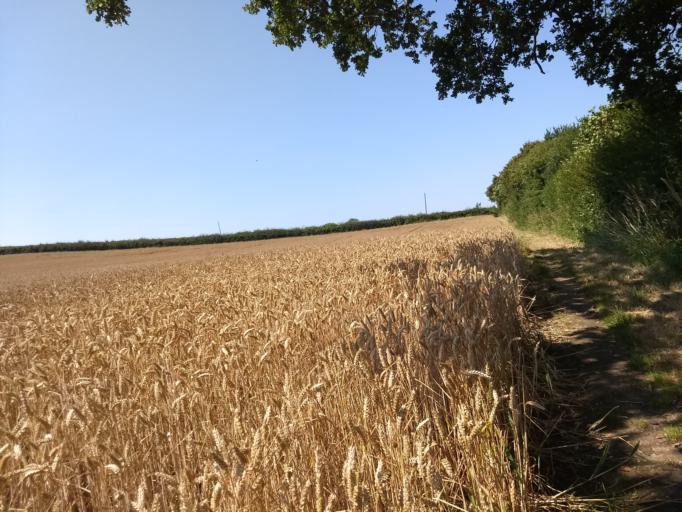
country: GB
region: England
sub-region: Isle of Wight
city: Newport
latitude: 50.6948
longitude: -1.3360
